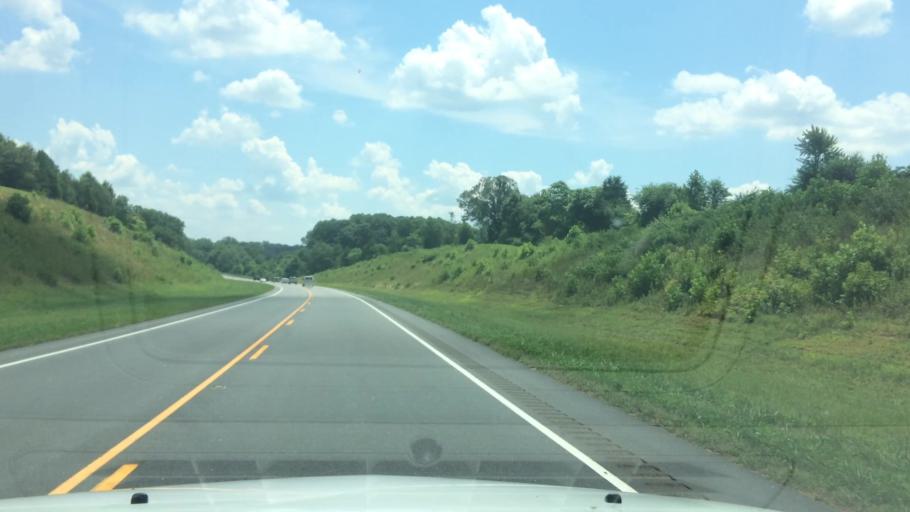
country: US
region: North Carolina
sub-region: Alexander County
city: Stony Point
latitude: 35.8662
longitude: -81.0616
